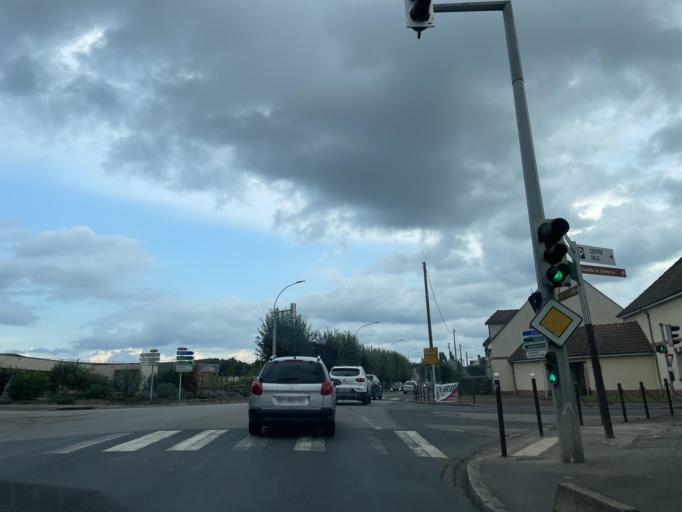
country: FR
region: Haute-Normandie
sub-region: Departement de la Seine-Maritime
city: Gournay-en-Bray
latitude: 49.4856
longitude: 1.7268
